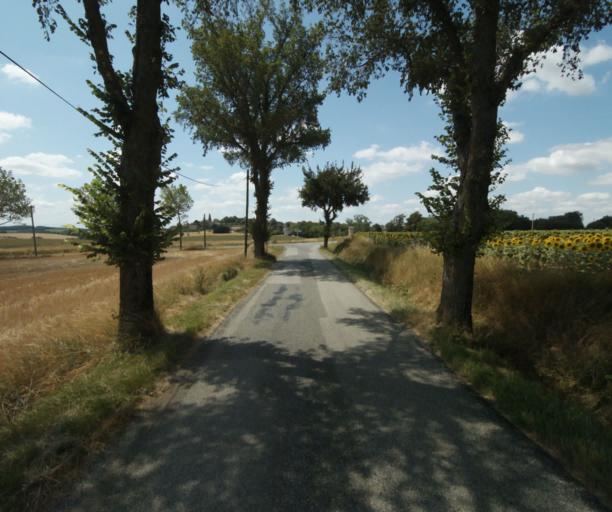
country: FR
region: Midi-Pyrenees
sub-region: Departement de la Haute-Garonne
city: Saint-Felix-Lauragais
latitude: 43.4621
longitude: 1.8397
